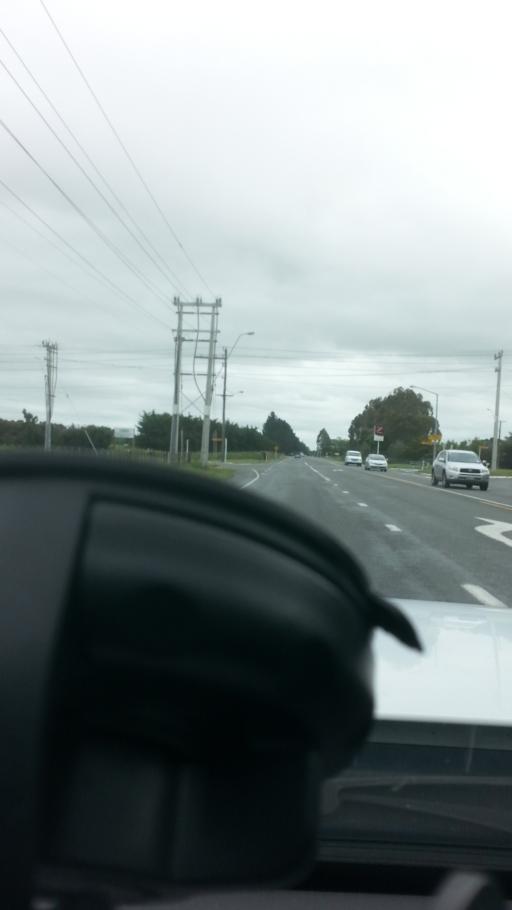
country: NZ
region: Wellington
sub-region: Masterton District
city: Masterton
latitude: -40.9690
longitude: 175.6032
